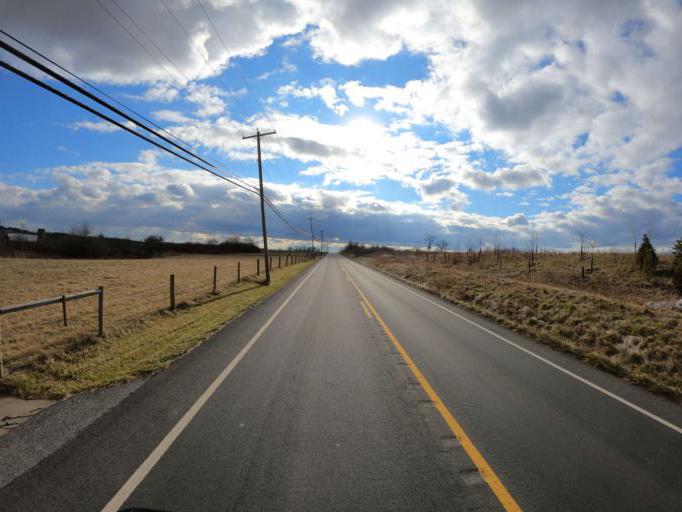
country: US
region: Maryland
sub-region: Carroll County
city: New Windsor
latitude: 39.5217
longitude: -77.1057
